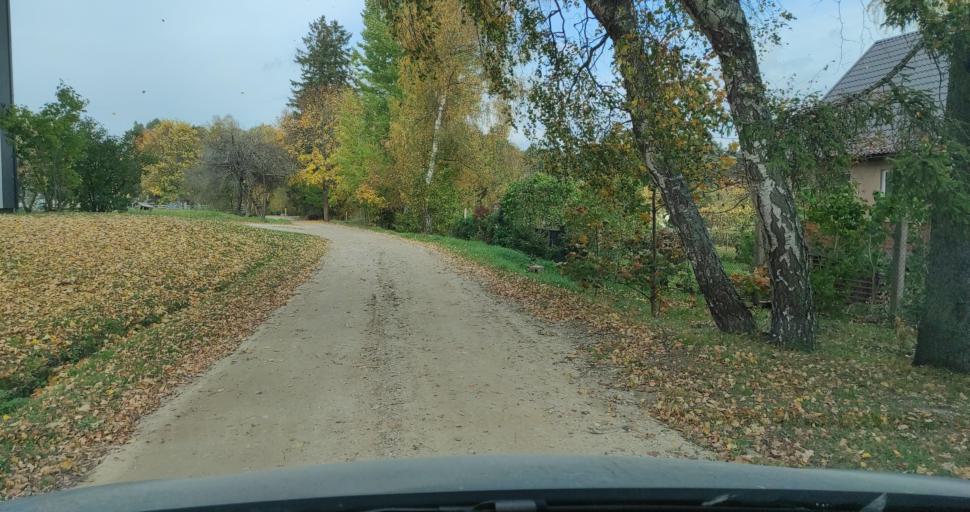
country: LV
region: Kuldigas Rajons
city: Kuldiga
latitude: 56.9611
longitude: 21.9218
